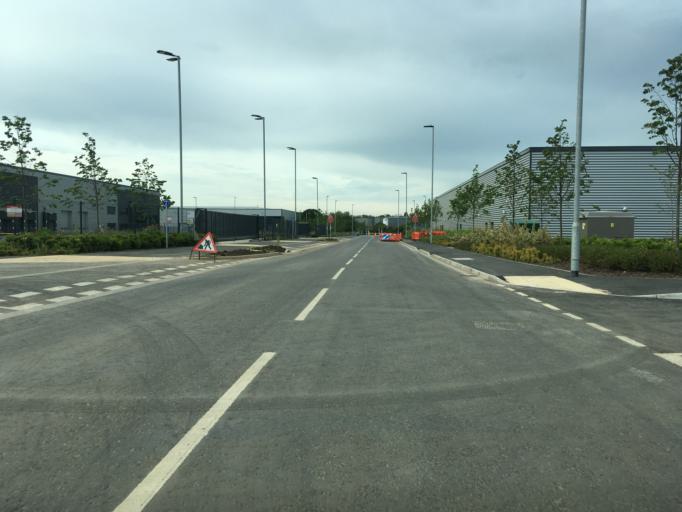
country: GB
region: England
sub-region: South Gloucestershire
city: Stoke Gifford
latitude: 51.5215
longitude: -2.5645
